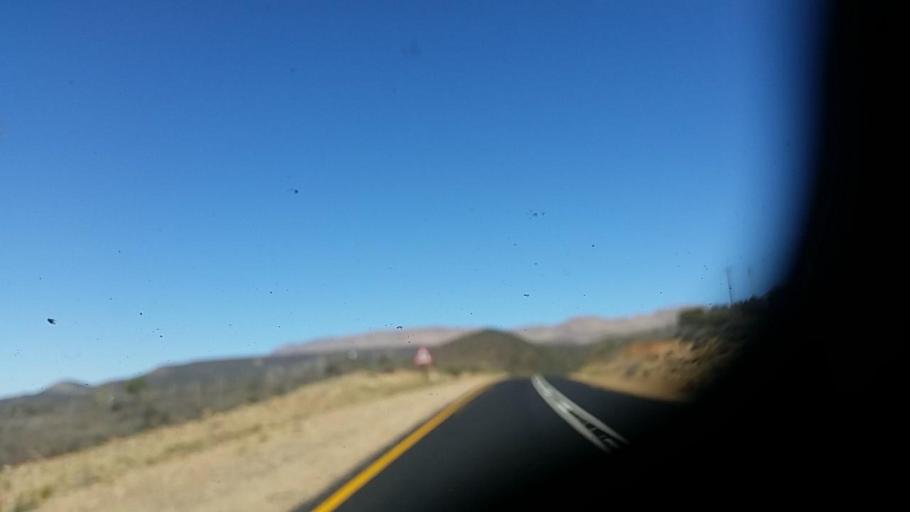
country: ZA
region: Western Cape
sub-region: Eden District Municipality
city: George
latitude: -33.5471
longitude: 22.7383
